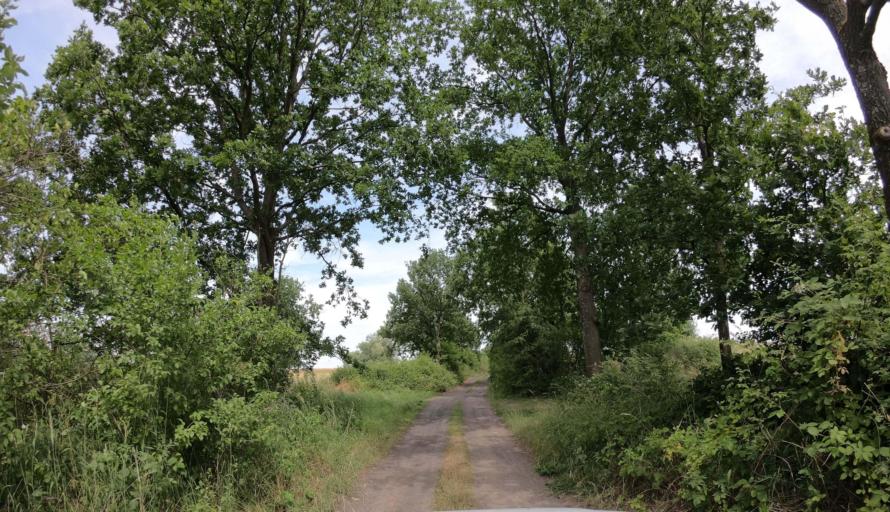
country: PL
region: West Pomeranian Voivodeship
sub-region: Powiat pyrzycki
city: Kozielice
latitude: 53.0333
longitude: 14.7602
